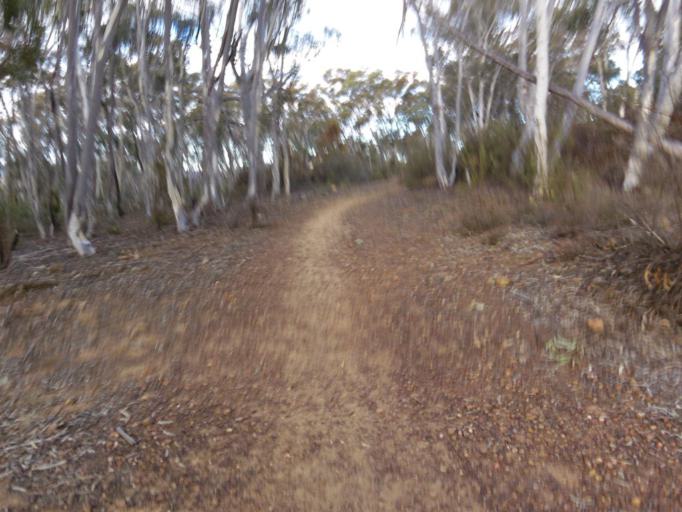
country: AU
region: Australian Capital Territory
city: Acton
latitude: -35.2607
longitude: 149.1096
